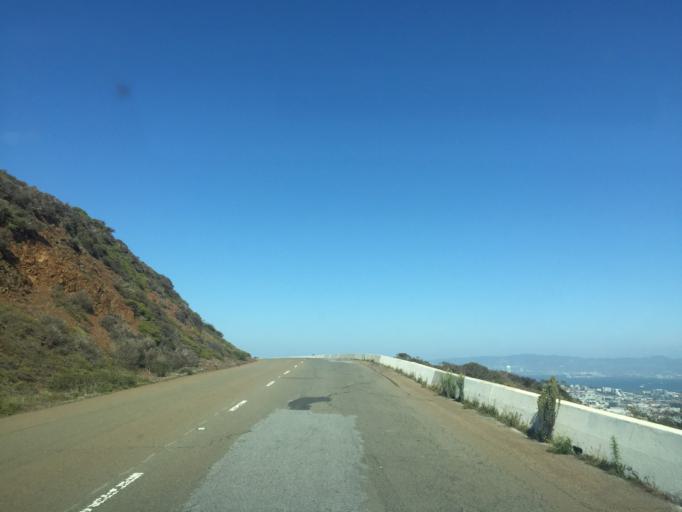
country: US
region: California
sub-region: San Francisco County
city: San Francisco
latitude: 37.7511
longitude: -122.4475
